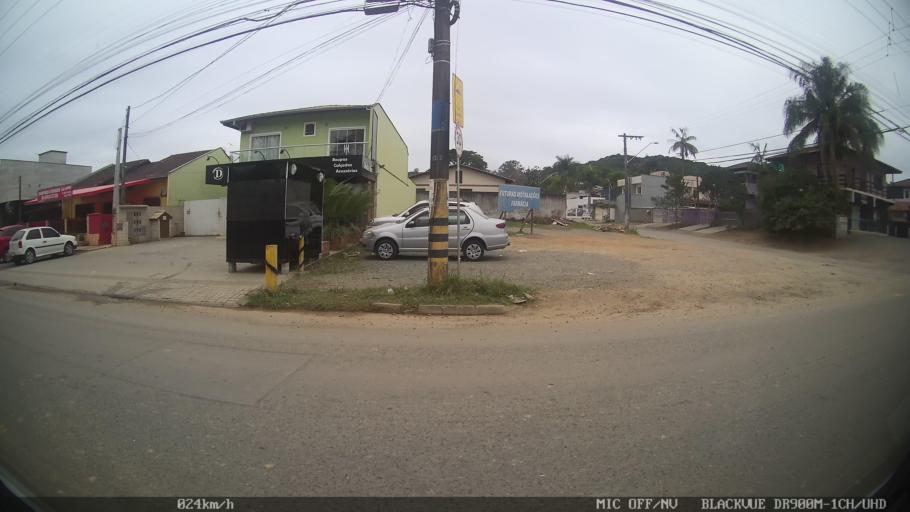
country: BR
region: Santa Catarina
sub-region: Joinville
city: Joinville
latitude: -26.3618
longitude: -48.8138
